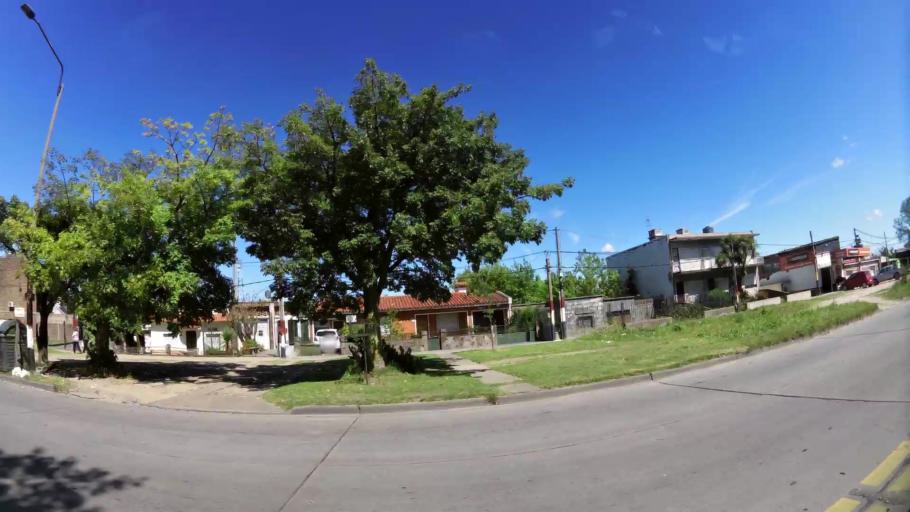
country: UY
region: Canelones
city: Paso de Carrasco
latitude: -34.8489
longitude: -56.1270
